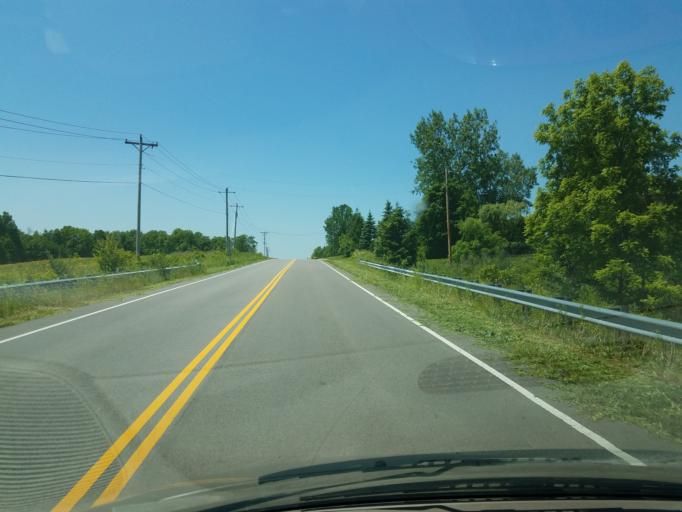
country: US
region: Ohio
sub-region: Delaware County
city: Sunbury
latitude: 40.2904
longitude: -82.8813
